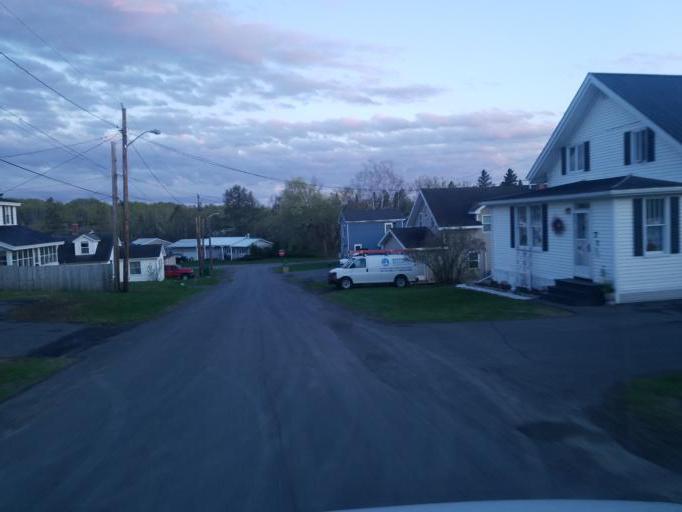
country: US
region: Maine
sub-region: Aroostook County
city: Caribou
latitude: 46.8593
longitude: -68.0221
